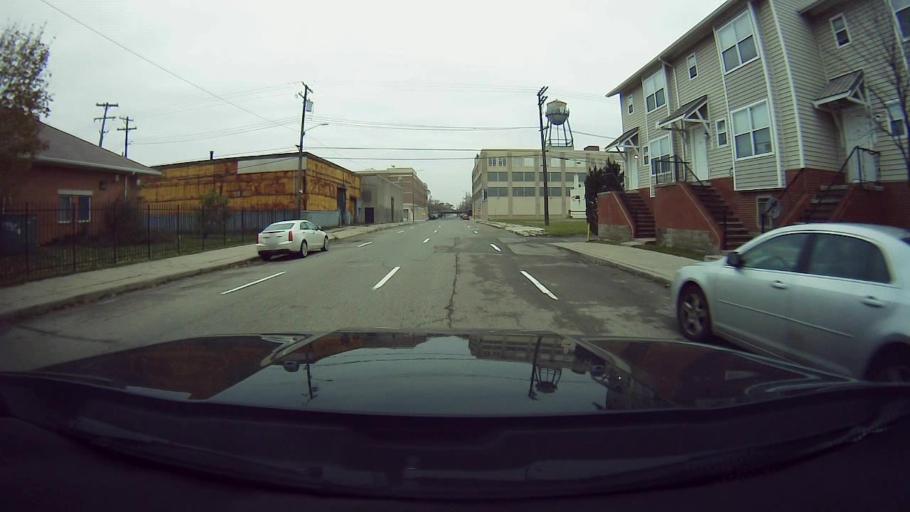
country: US
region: Michigan
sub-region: Wayne County
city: Hamtramck
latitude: 42.3673
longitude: -83.0656
